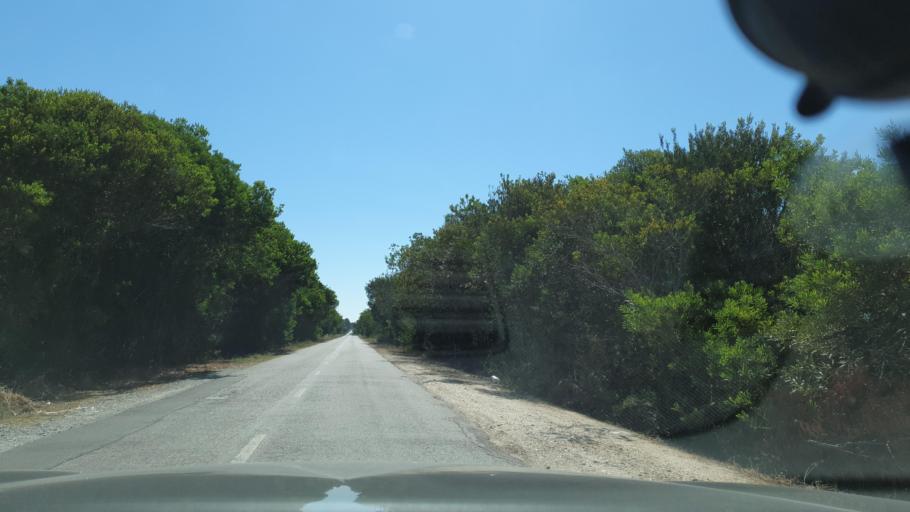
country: PT
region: Beja
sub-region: Odemira
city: Sao Teotonio
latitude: 37.5006
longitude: -8.6809
